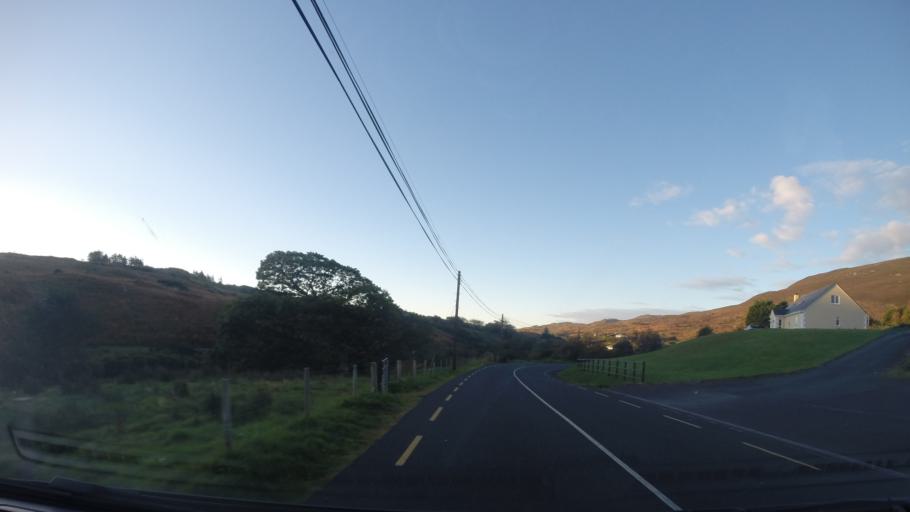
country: IE
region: Ulster
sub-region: County Donegal
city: Killybegs
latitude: 54.6543
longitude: -8.6378
